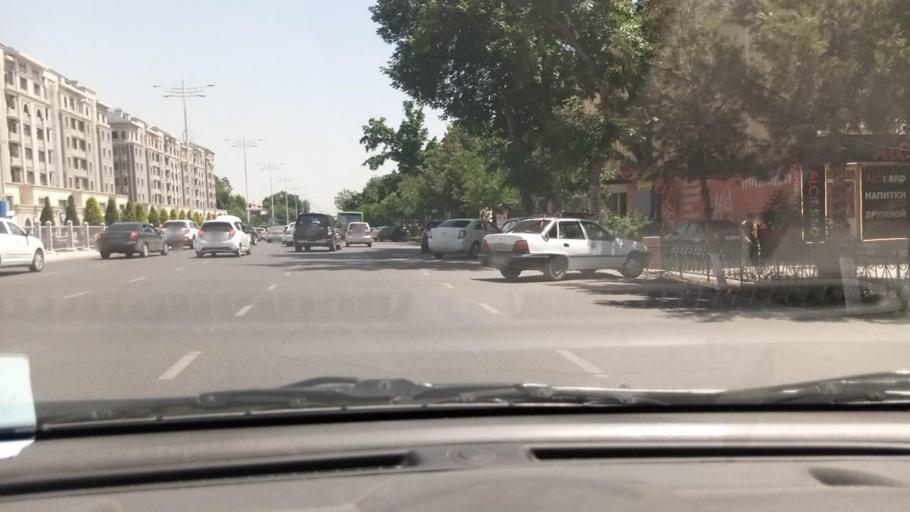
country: UZ
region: Toshkent Shahri
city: Tashkent
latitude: 41.2900
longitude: 69.2264
